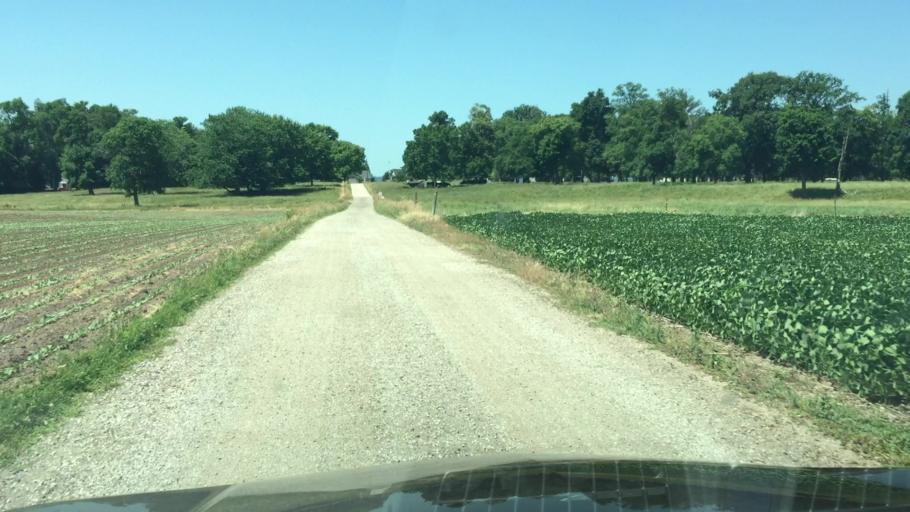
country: US
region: Wisconsin
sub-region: Fond du Lac County
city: Saint Peter
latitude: 43.9604
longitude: -88.3149
